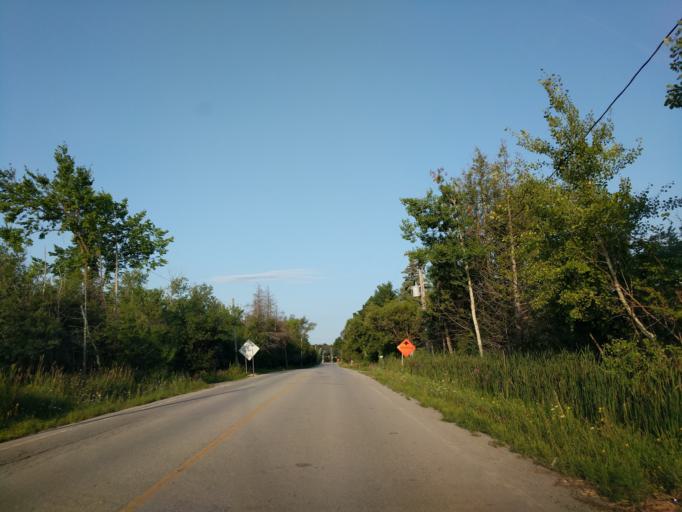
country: CA
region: Ontario
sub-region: York
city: Richmond Hill
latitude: 43.9123
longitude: -79.4182
